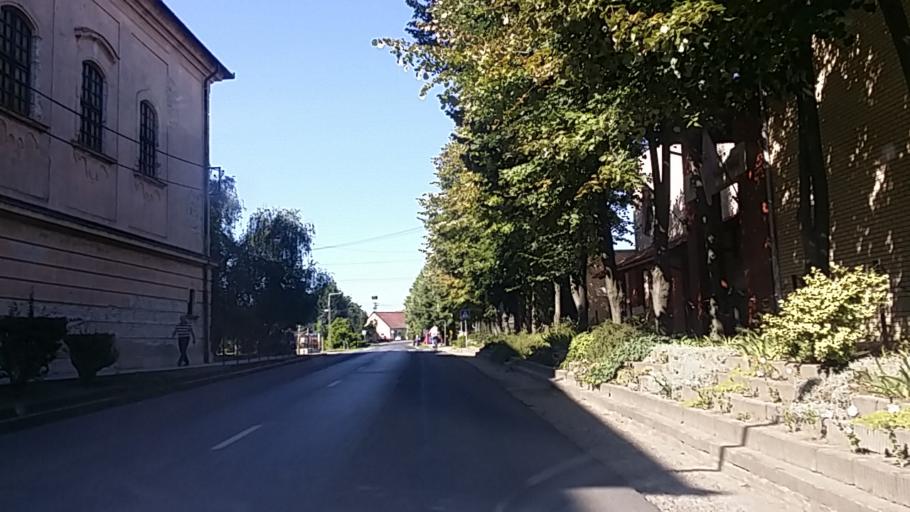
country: HU
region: Fejer
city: Mezofalva
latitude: 46.9326
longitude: 18.7792
